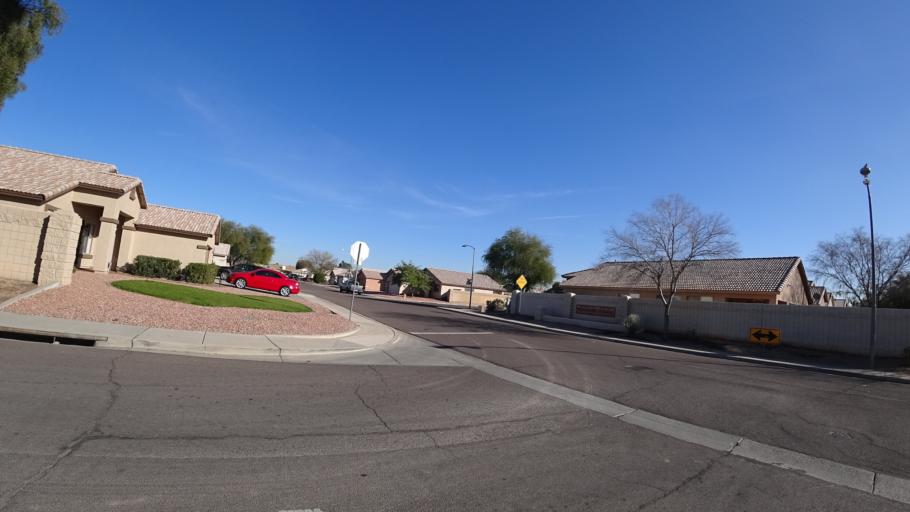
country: US
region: Arizona
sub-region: Maricopa County
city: Glendale
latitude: 33.5191
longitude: -112.2291
